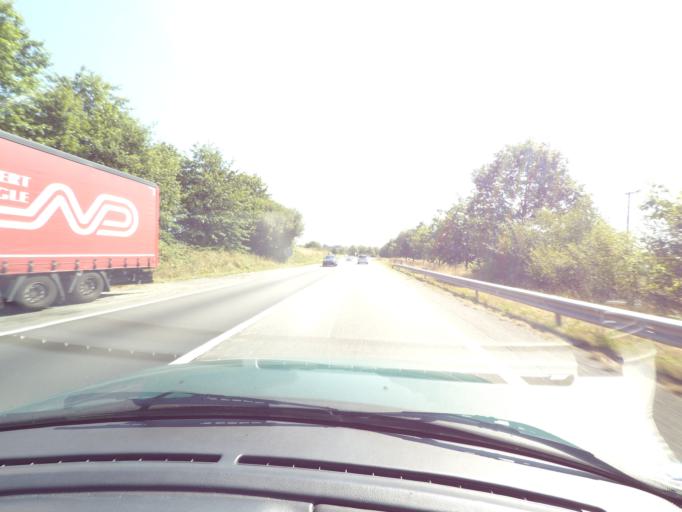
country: FR
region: Limousin
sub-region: Departement de la Haute-Vienne
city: Chaptelat
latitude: 45.8907
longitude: 1.2757
